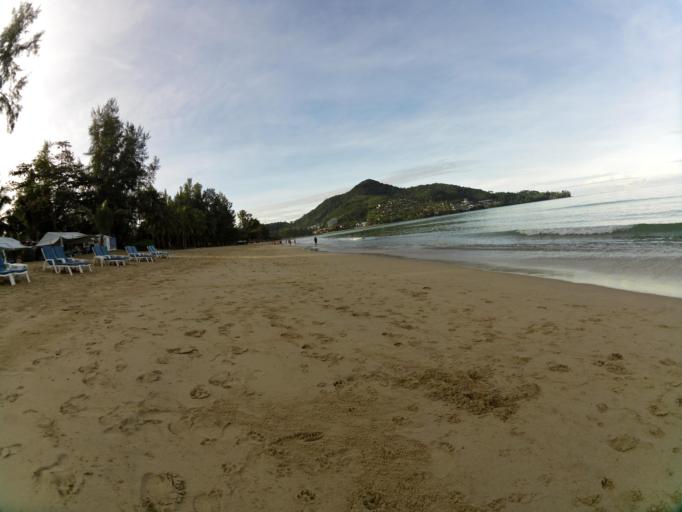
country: TH
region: Phuket
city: Patong
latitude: 7.9586
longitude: 98.2837
